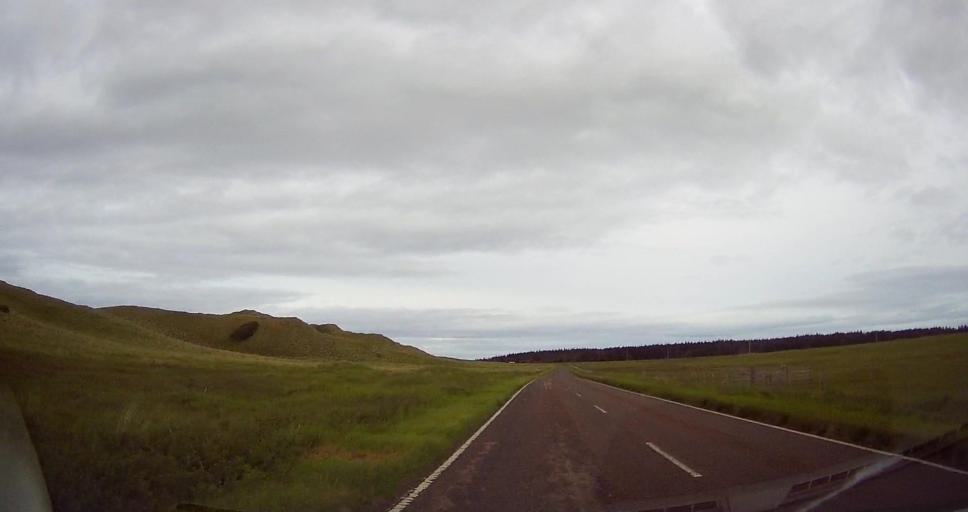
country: GB
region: Scotland
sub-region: Highland
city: Thurso
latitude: 58.6035
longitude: -3.3477
